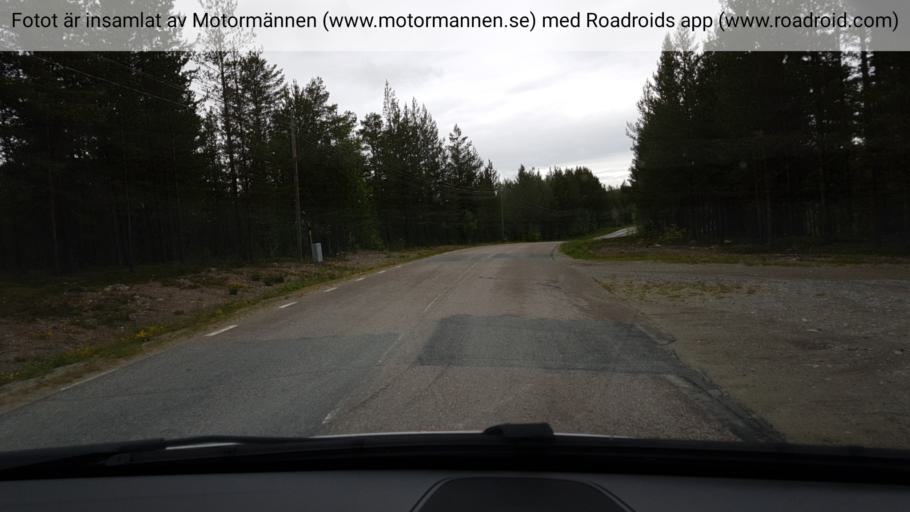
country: SE
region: Jaemtland
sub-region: Harjedalens Kommun
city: Sveg
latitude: 62.4022
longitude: 13.5219
